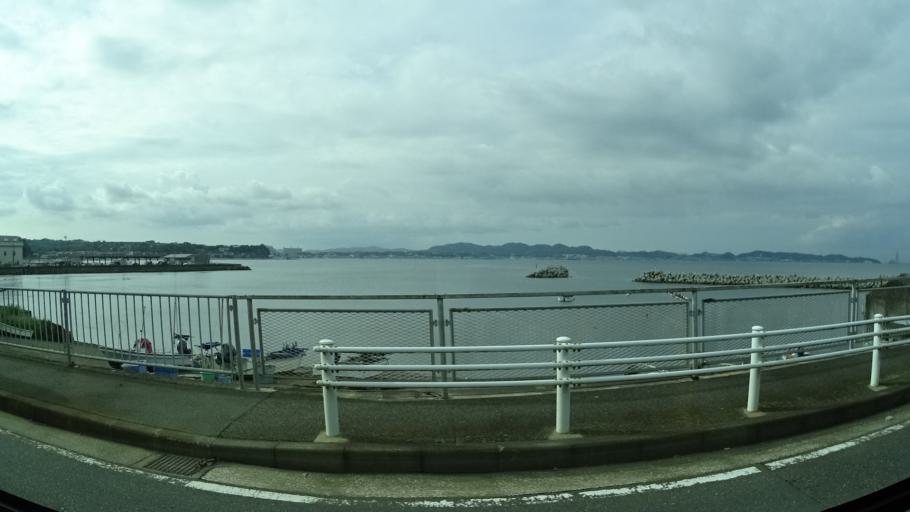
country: JP
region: Kanagawa
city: Miura
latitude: 35.1575
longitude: 139.6689
